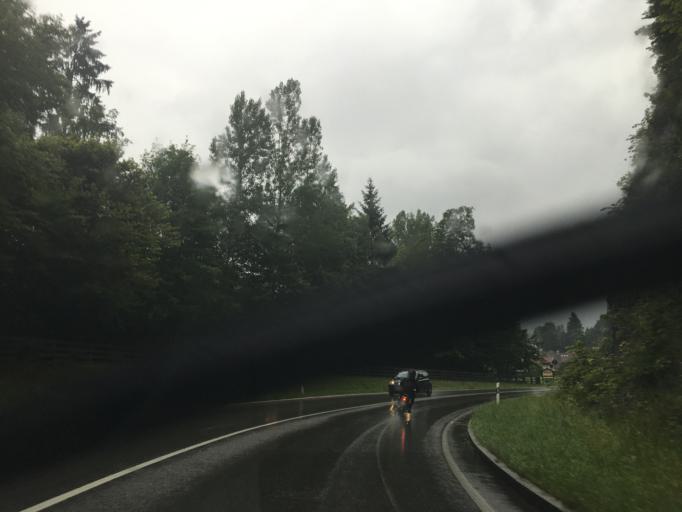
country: DE
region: Bavaria
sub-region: Upper Bavaria
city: Unterwossen
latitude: 47.7183
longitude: 12.4778
